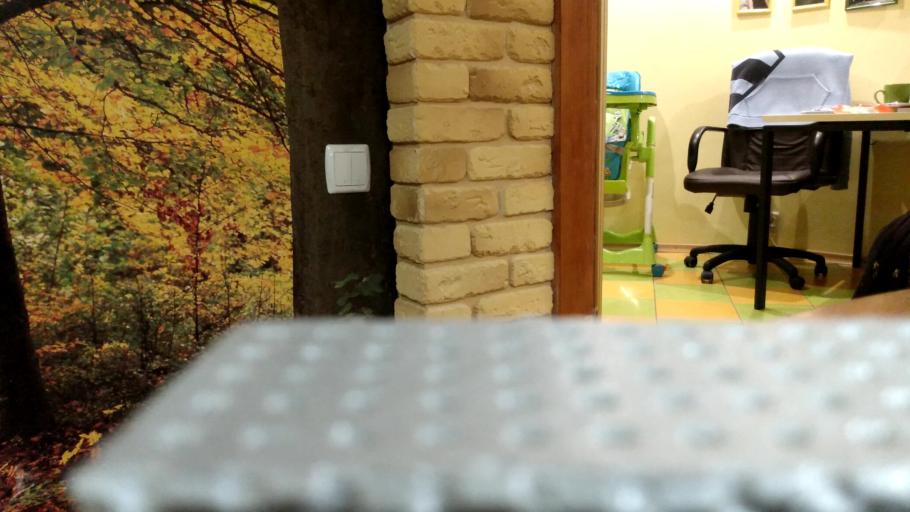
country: RU
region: Republic of Karelia
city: Pudozh
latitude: 61.8829
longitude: 37.6418
